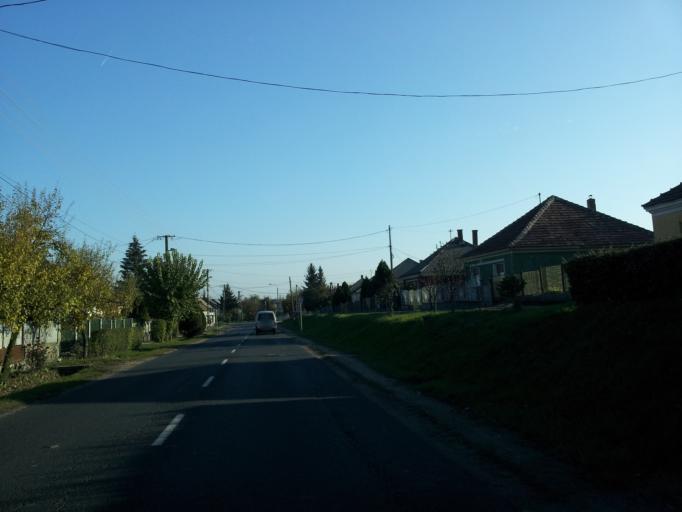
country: HU
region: Fejer
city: Bodajk
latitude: 47.3172
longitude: 18.2472
